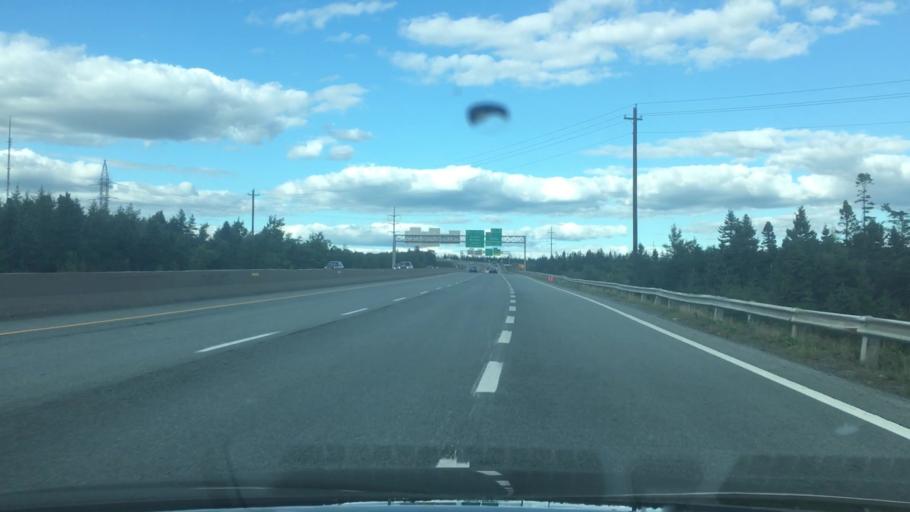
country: CA
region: Nova Scotia
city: Halifax
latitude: 44.6375
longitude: -63.6607
